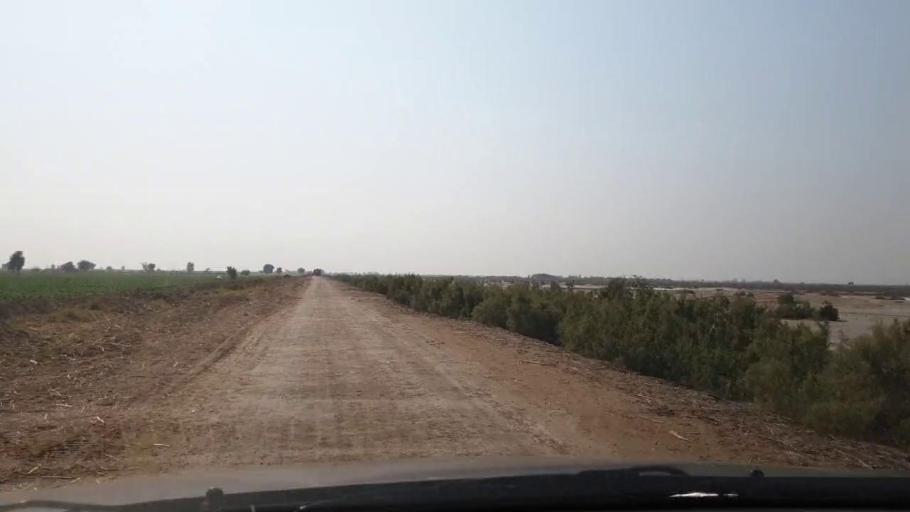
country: PK
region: Sindh
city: Jhol
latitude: 25.8605
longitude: 68.9940
